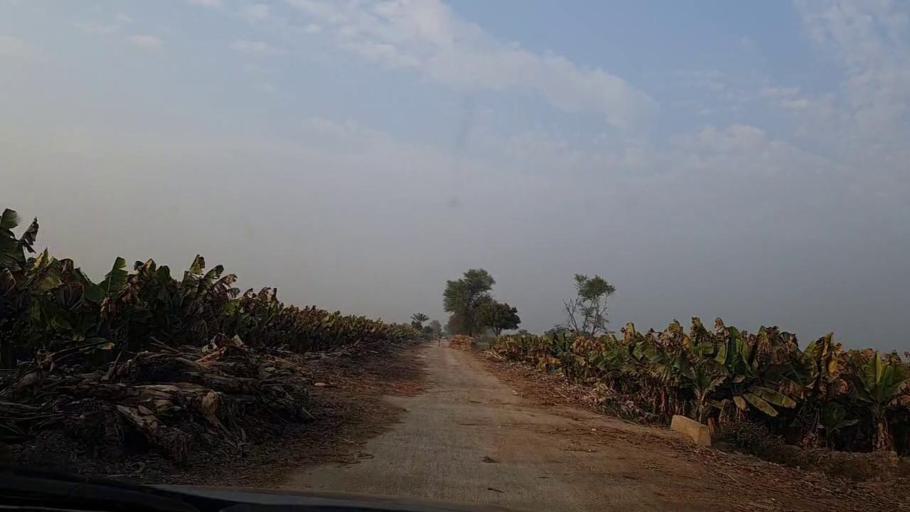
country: PK
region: Sindh
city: Nawabshah
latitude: 26.2900
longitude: 68.2854
